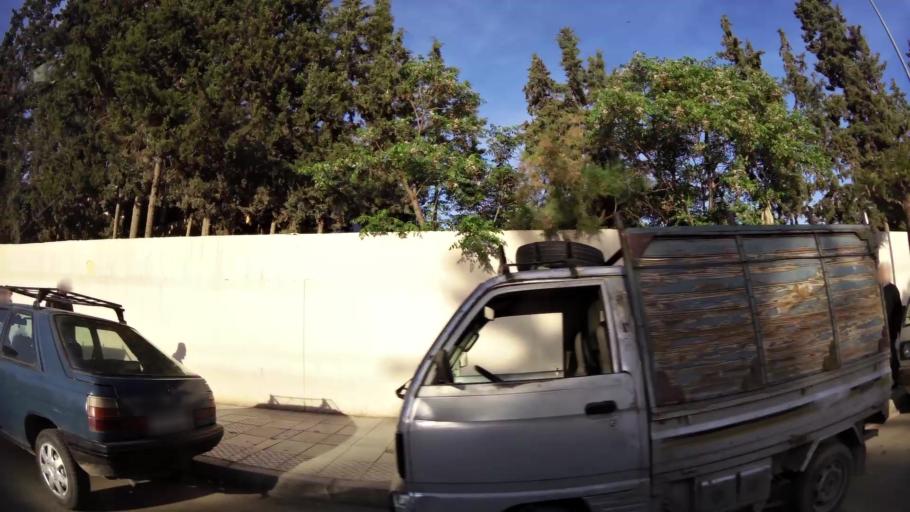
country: MA
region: Oriental
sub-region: Oujda-Angad
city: Oujda
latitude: 34.6780
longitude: -1.9081
